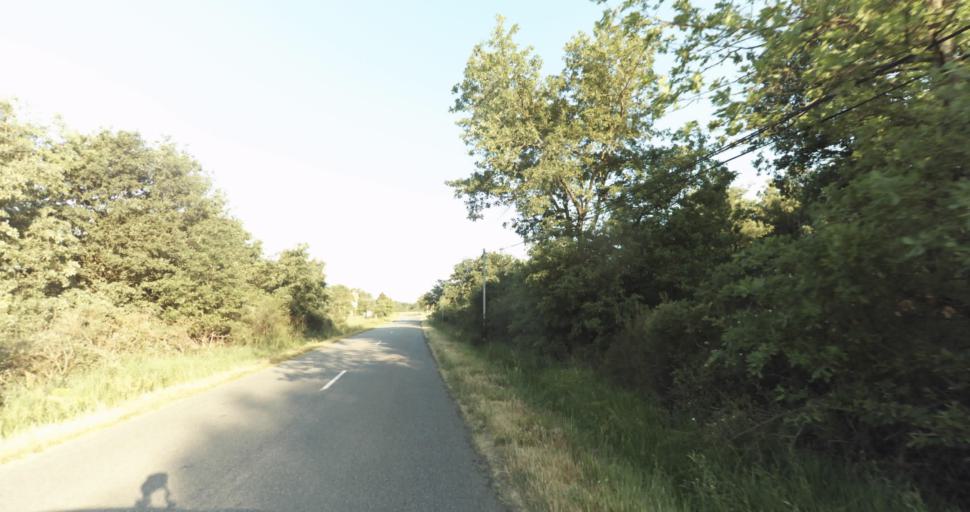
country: FR
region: Midi-Pyrenees
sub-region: Departement de la Haute-Garonne
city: Fontenilles
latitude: 43.5457
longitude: 1.2076
